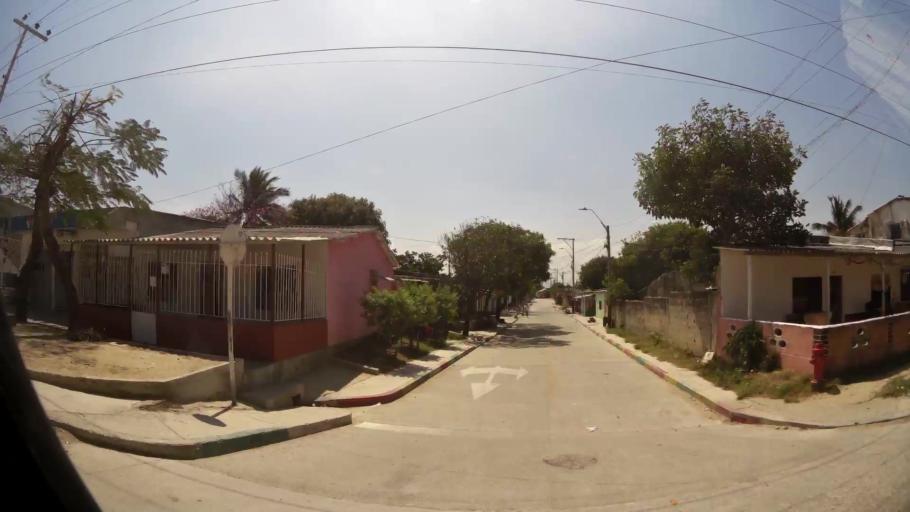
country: CO
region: Atlantico
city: Barranquilla
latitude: 10.9698
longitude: -74.8320
